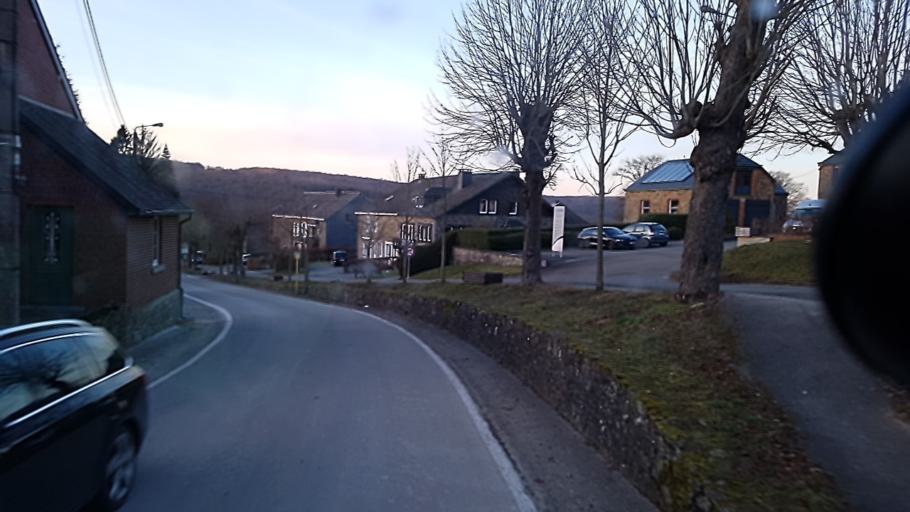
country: BE
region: Wallonia
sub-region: Province du Luxembourg
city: Daverdisse
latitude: 50.0216
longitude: 5.1180
